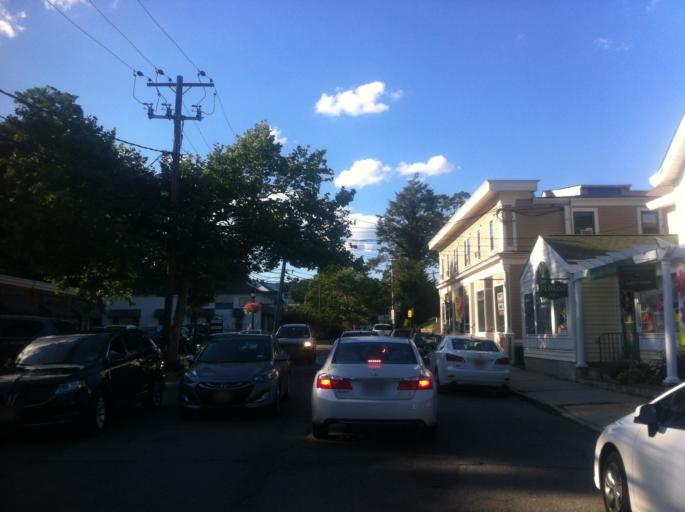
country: US
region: New York
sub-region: Nassau County
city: Locust Valley
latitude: 40.8763
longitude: -73.5972
